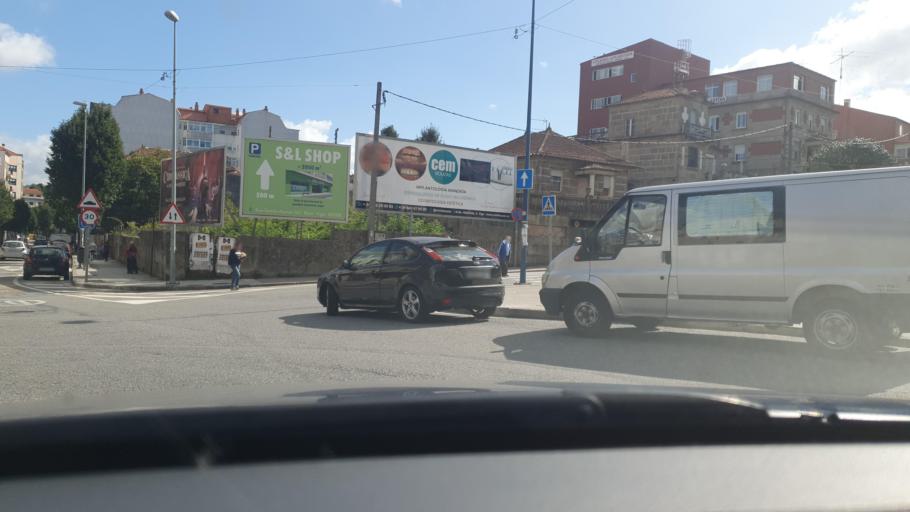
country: ES
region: Galicia
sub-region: Provincia de Pontevedra
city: Vigo
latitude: 42.2223
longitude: -8.7527
